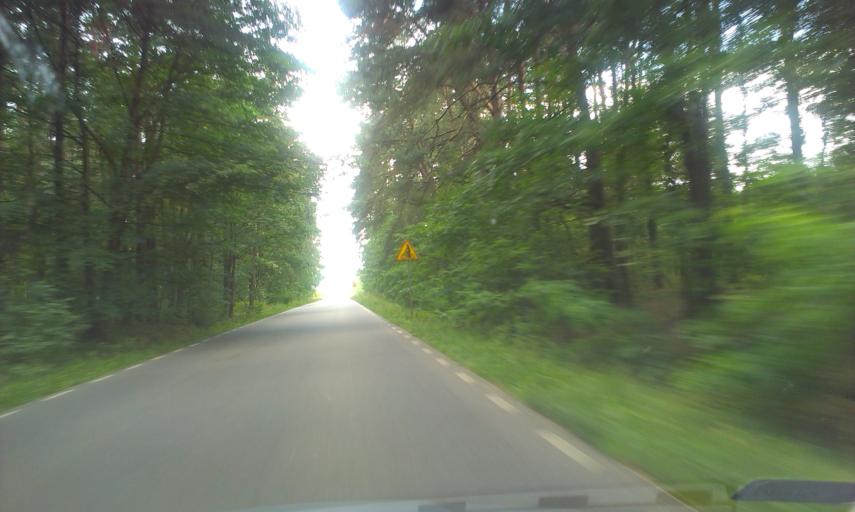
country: PL
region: Masovian Voivodeship
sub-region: Powiat zyrardowski
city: Radziejowice
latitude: 51.9688
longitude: 20.5848
